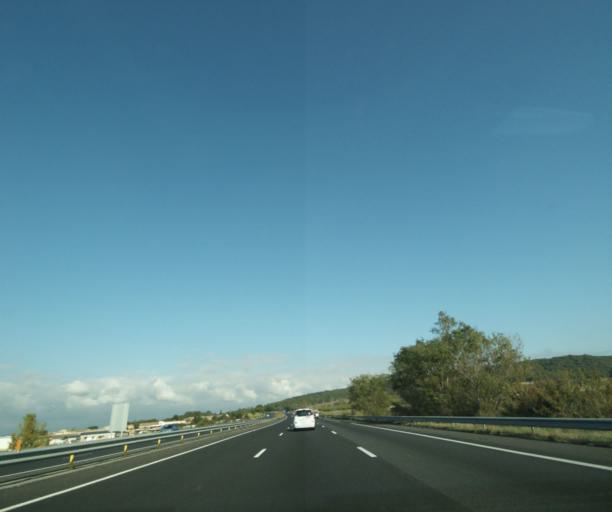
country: FR
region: Languedoc-Roussillon
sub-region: Departement de l'Aude
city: Vinassan
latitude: 43.1937
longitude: 3.0720
